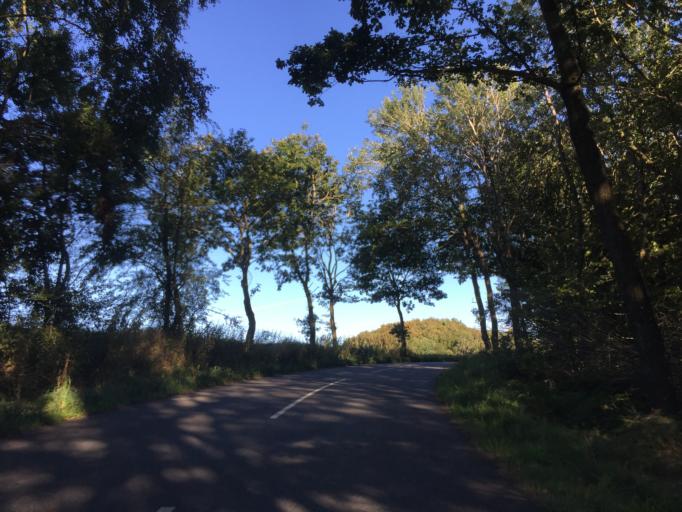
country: DK
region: Central Jutland
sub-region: Silkeborg Kommune
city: Svejbaek
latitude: 56.2225
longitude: 9.6917
